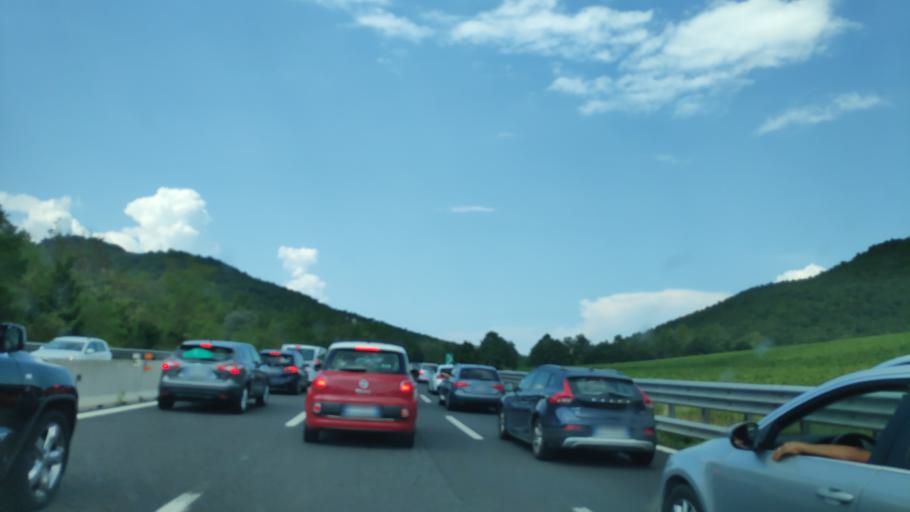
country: IT
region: Umbria
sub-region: Provincia di Terni
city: Stazione di Allerona
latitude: 42.8071
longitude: 12.0368
